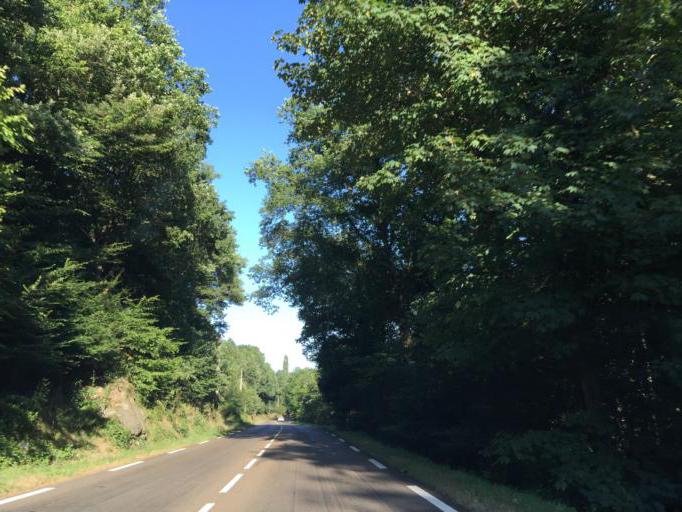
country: FR
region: Rhone-Alpes
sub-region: Departement de la Loire
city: Sorbiers
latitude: 45.4742
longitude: 4.4788
